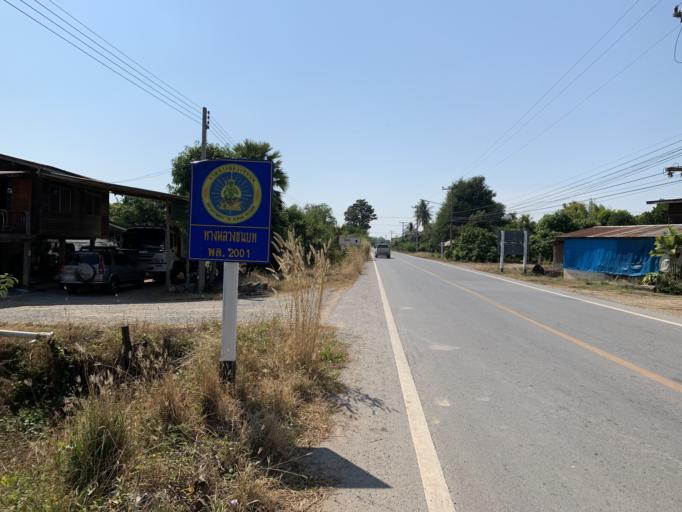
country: TH
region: Phitsanulok
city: Wang Thong
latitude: 16.7499
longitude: 100.3919
